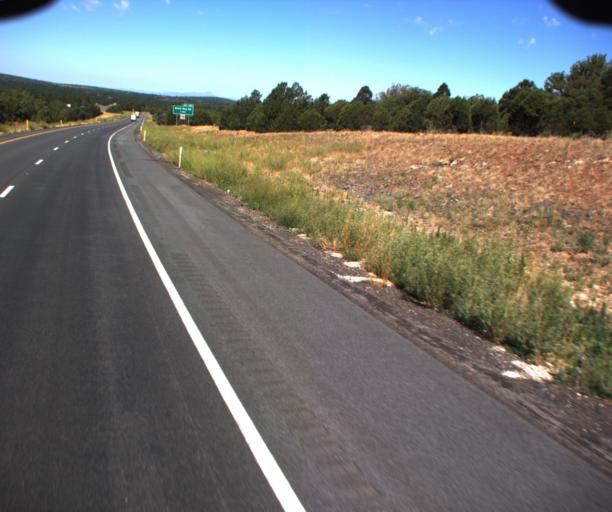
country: US
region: Arizona
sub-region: Coconino County
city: Williams
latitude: 35.2229
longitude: -112.2576
